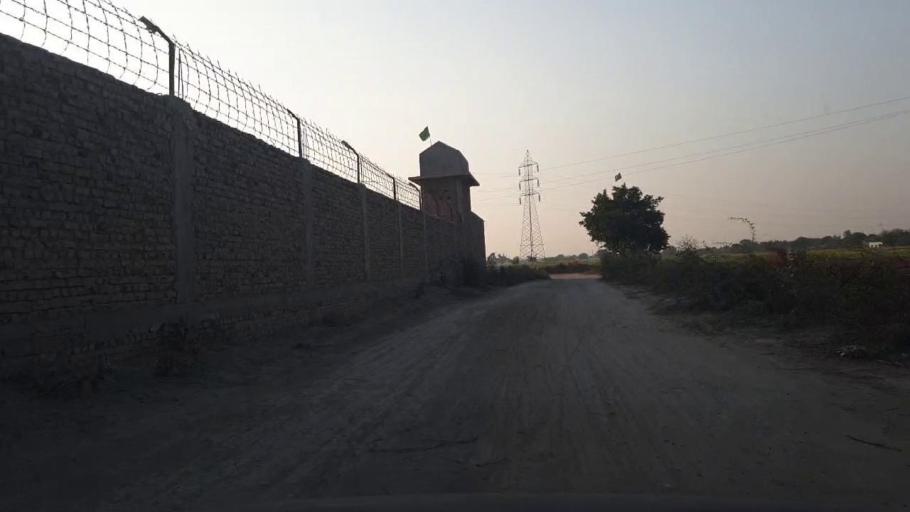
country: PK
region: Sindh
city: Hala
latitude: 25.8702
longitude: 68.4076
